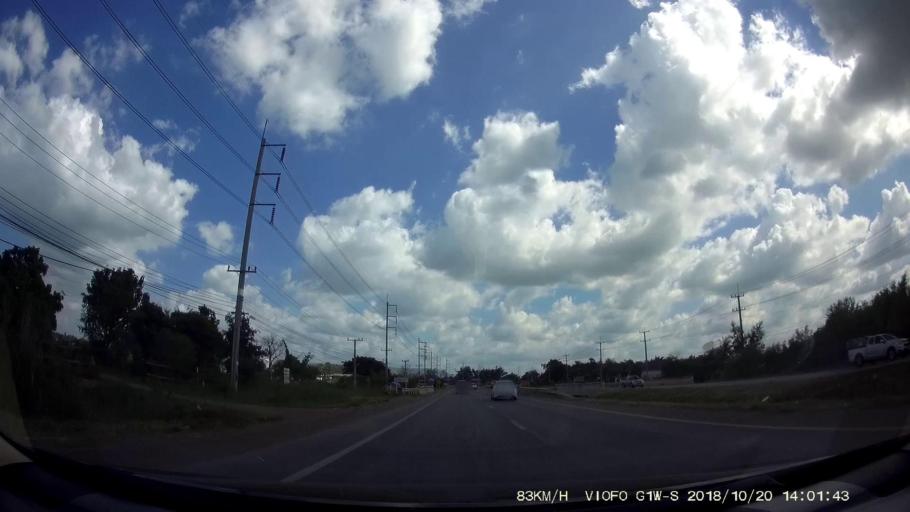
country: TH
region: Khon Kaen
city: Chum Phae
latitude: 16.4994
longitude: 102.1227
